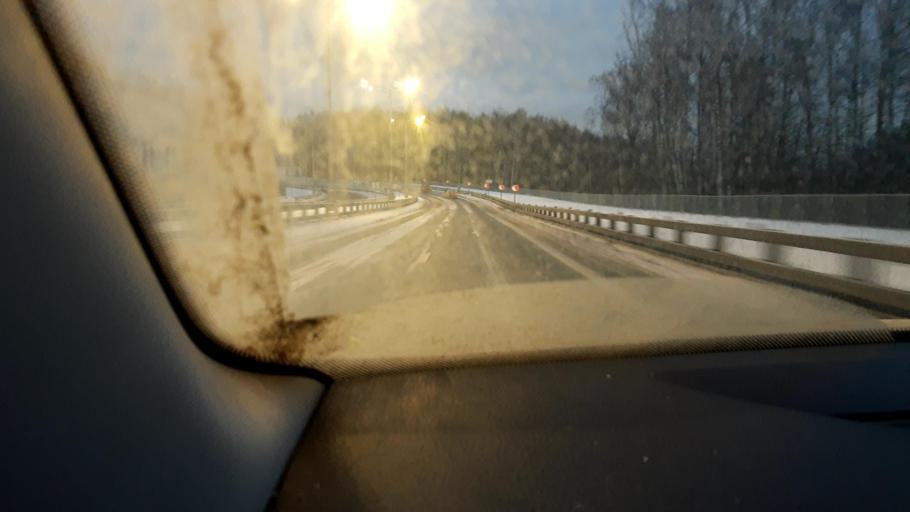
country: RU
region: Moscow
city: Tyoply Stan
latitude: 55.5999
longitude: 37.4969
